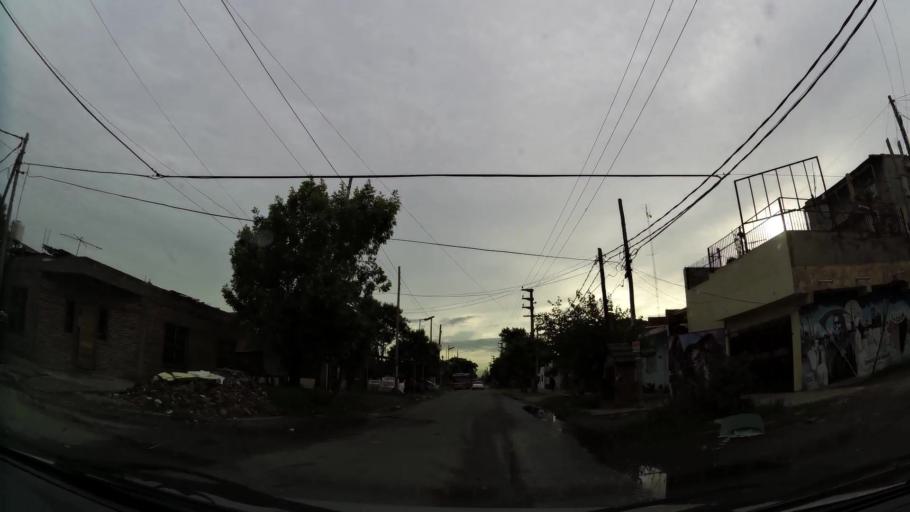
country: AR
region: Buenos Aires
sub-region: Partido de Lanus
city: Lanus
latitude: -34.7276
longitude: -58.3382
